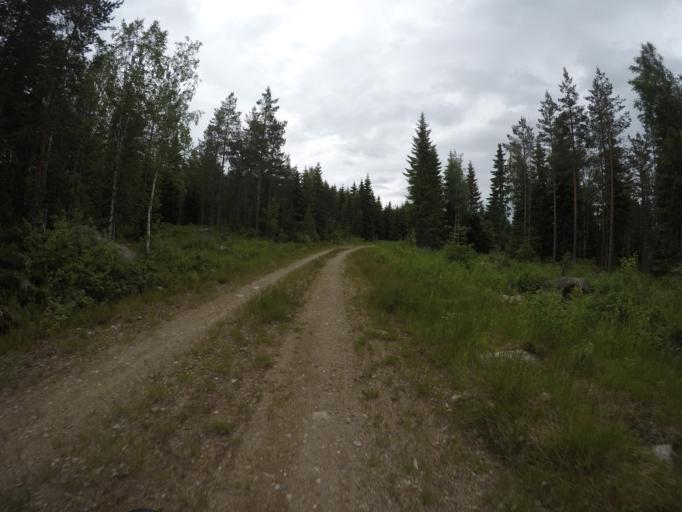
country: SE
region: Dalarna
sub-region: Ludvika Kommun
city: Abborrberget
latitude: 60.0618
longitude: 14.5629
